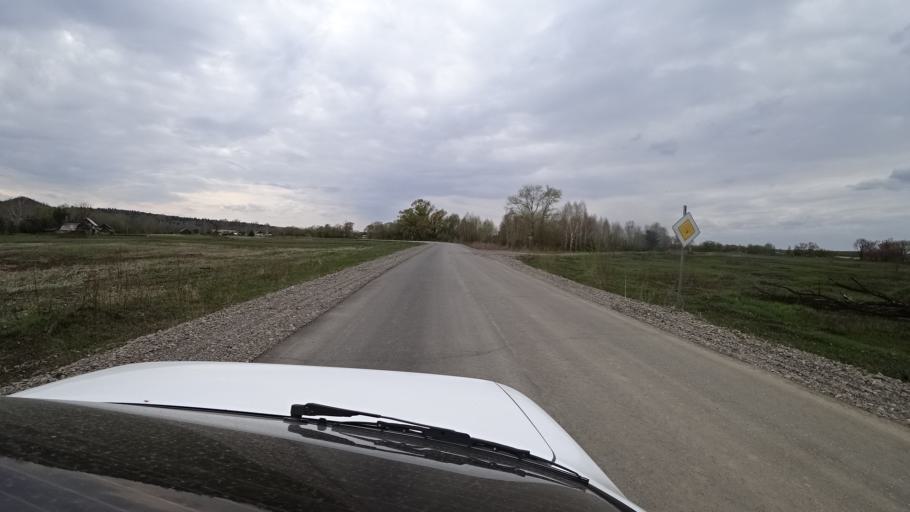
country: RU
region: Primorskiy
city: Novopokrovka
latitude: 45.4916
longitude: 134.4543
